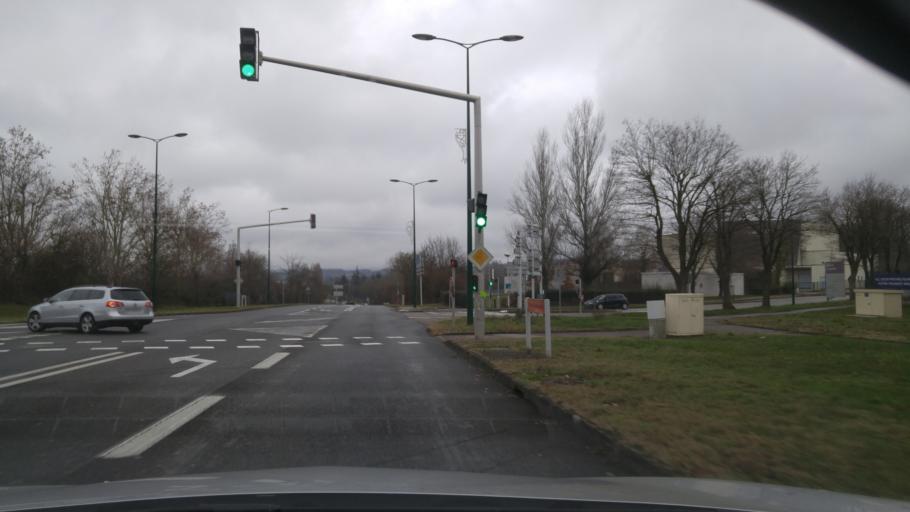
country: FR
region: Rhone-Alpes
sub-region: Departement de l'Isere
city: Villefontaine
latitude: 45.6188
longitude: 5.1455
